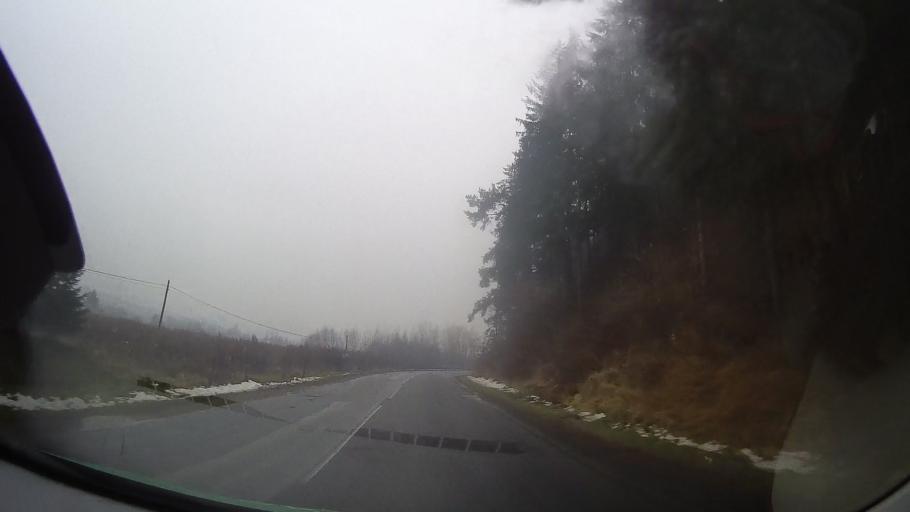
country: RO
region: Harghita
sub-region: Municipiul Gheorgheni
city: Gheorgheni
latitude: 46.7318
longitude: 25.6460
